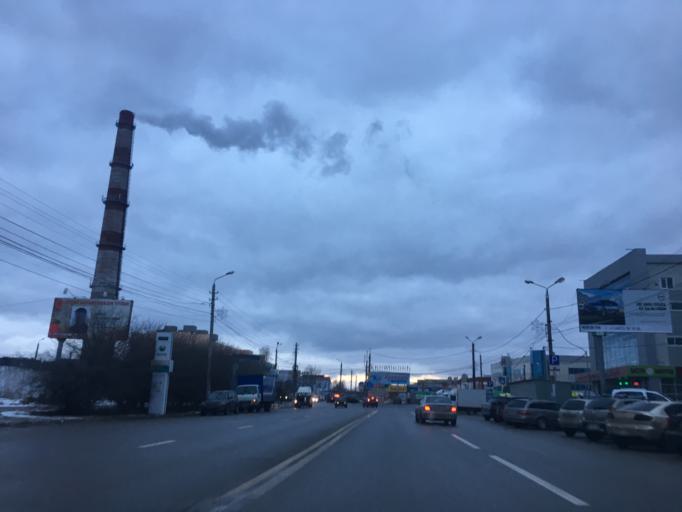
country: RU
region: Tula
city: Tula
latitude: 54.2004
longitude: 37.5914
